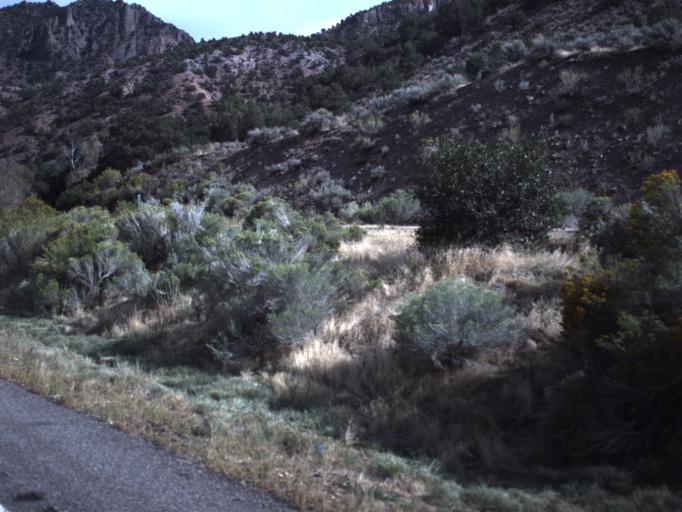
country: US
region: Utah
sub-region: Sevier County
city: Monroe
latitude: 38.5685
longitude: -112.2605
